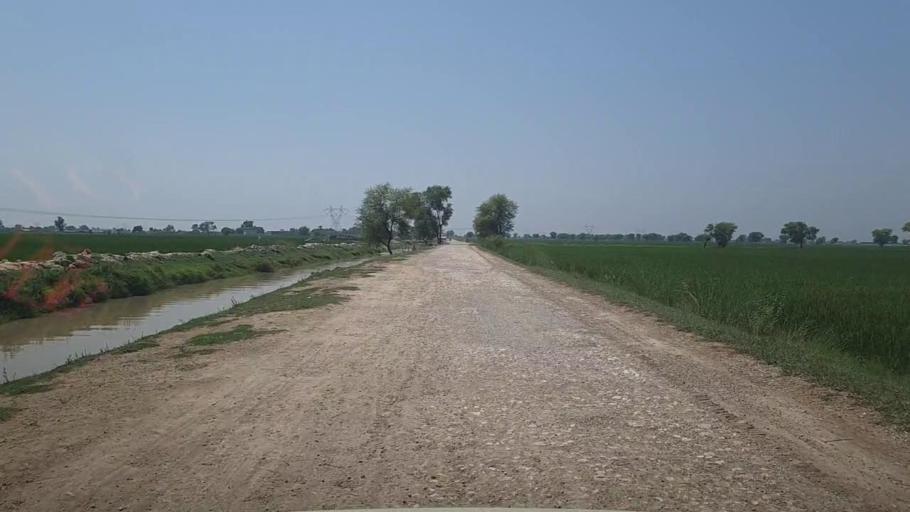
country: PK
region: Sindh
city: Kashmor
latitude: 28.3301
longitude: 69.3871
